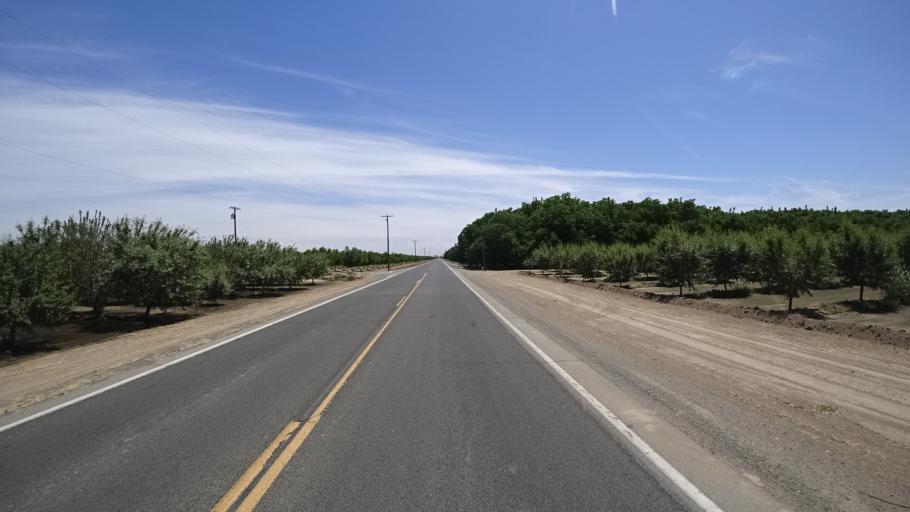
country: US
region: California
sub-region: Kings County
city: Lemoore
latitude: 36.3426
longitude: -119.7678
